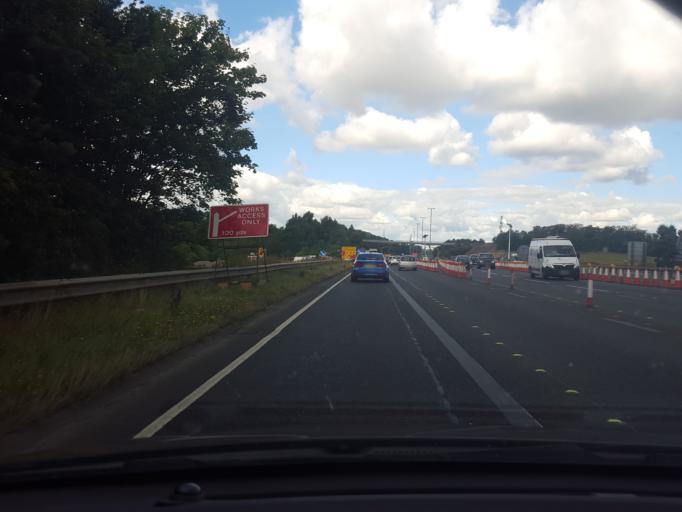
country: GB
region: Scotland
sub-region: South Lanarkshire
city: Bothwell
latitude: 55.8037
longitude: -4.0550
